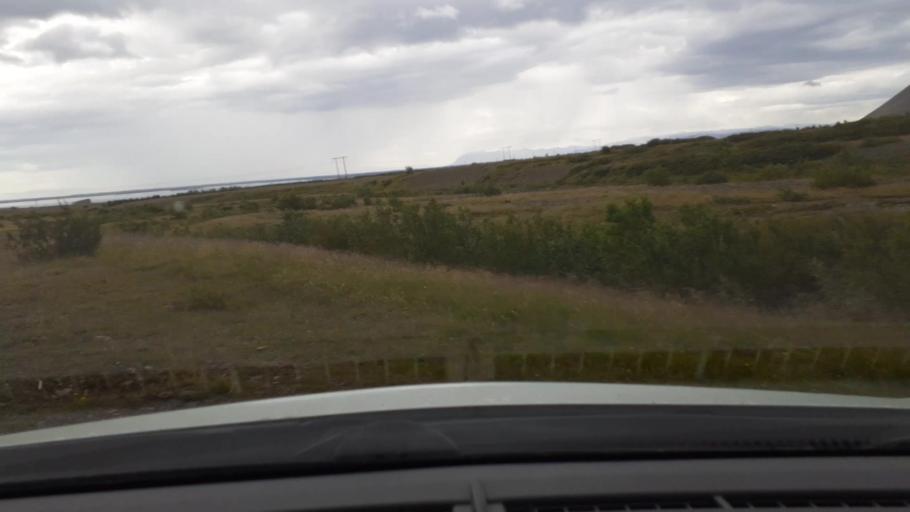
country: IS
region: West
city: Borgarnes
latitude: 64.4608
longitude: -21.9539
